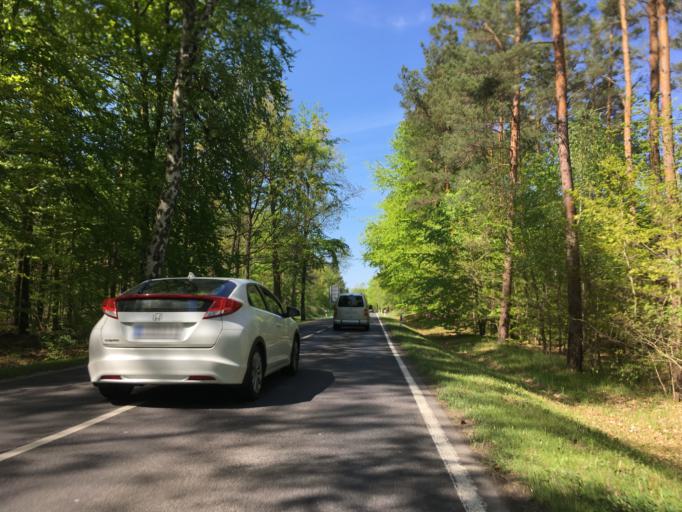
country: DE
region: Brandenburg
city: Marienwerder
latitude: 52.7752
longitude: 13.5615
